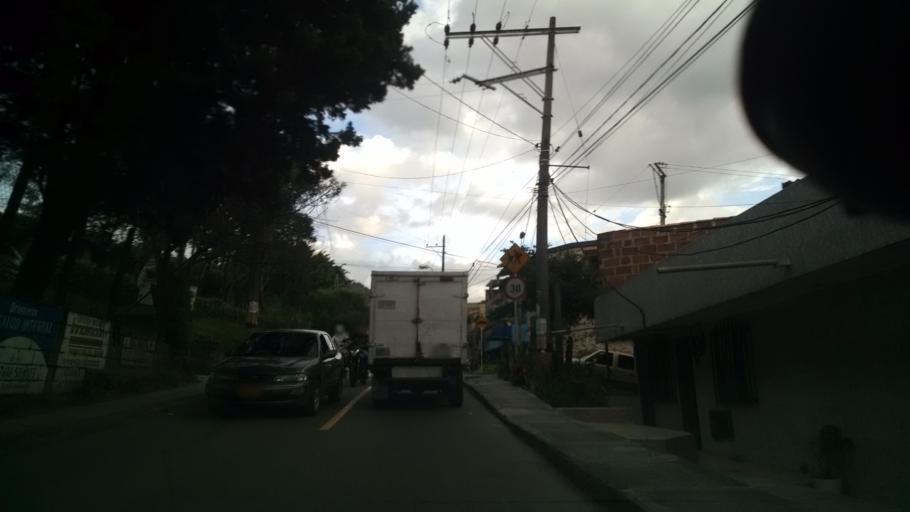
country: CO
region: Antioquia
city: Medellin
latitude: 6.2838
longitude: -75.5915
